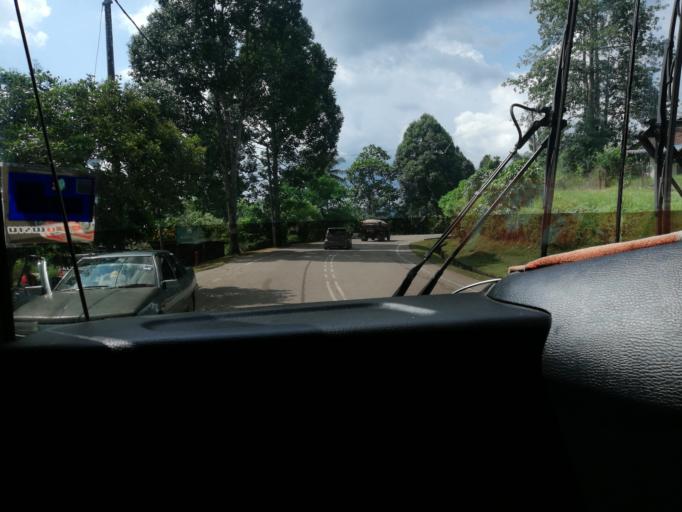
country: MY
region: Penang
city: Nibong Tebal
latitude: 5.2171
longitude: 100.6097
